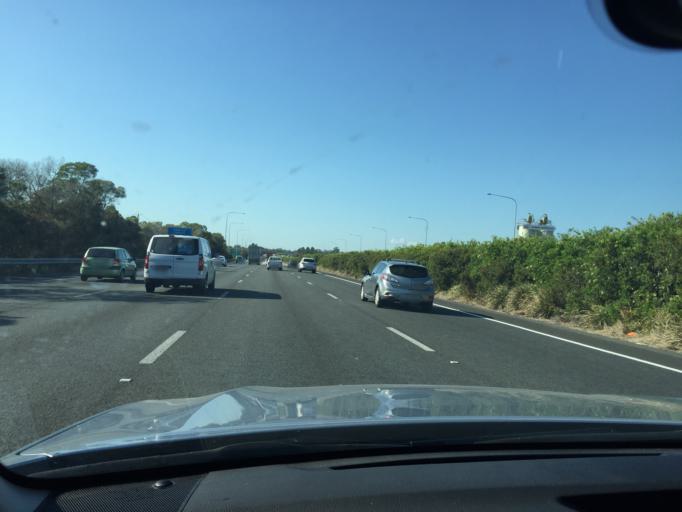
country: AU
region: Queensland
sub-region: Gold Coast
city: Yatala
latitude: -27.7288
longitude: 153.2234
